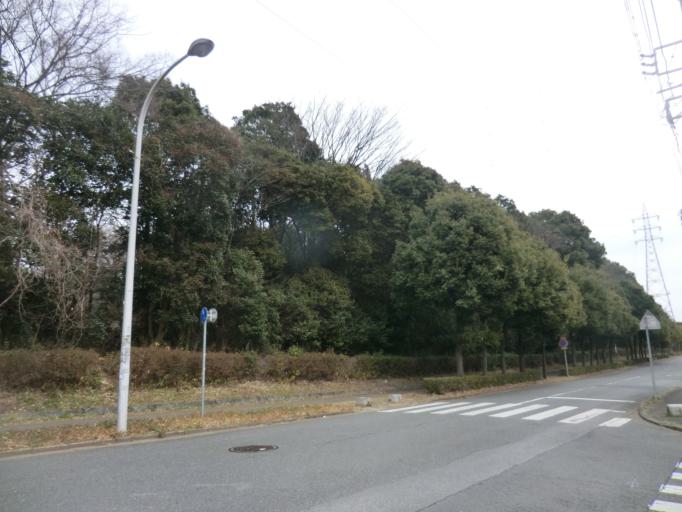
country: JP
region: Ibaraki
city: Naka
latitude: 36.0990
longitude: 140.1076
